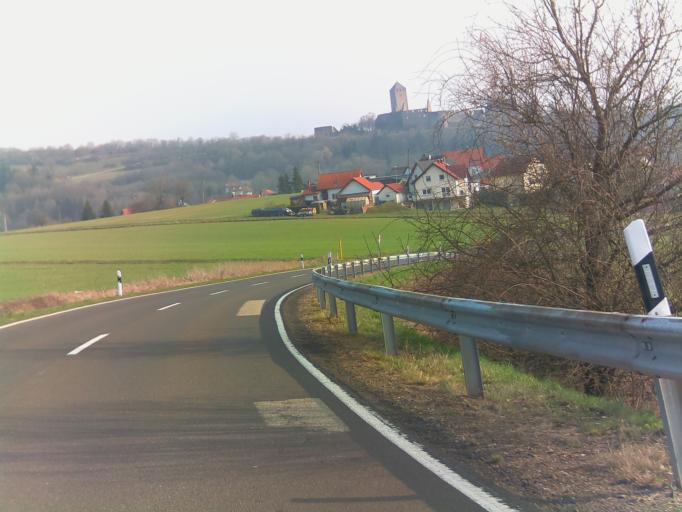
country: DE
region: Rheinland-Pfalz
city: Thallichtenberg
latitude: 49.5636
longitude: 7.3478
